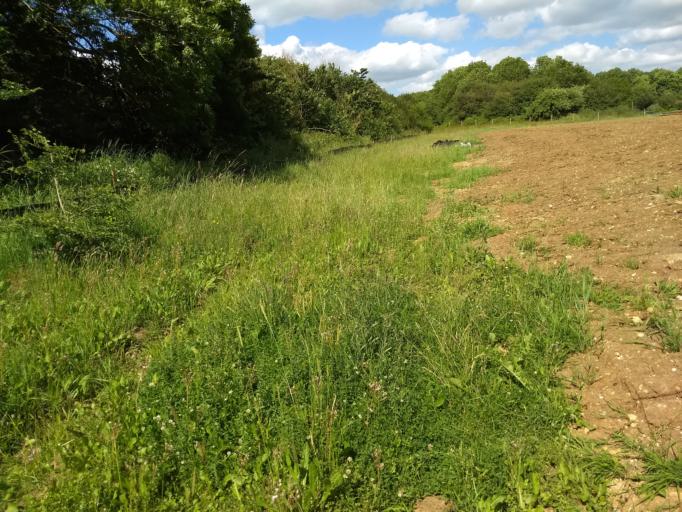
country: GB
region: England
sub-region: Milton Keynes
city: Calverton
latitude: 52.0488
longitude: -0.8413
